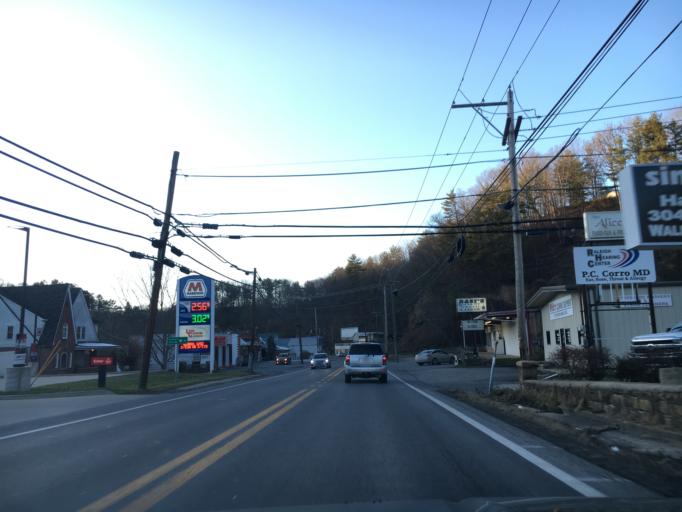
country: US
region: West Virginia
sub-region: Raleigh County
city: Beaver
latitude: 37.7504
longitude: -81.1418
